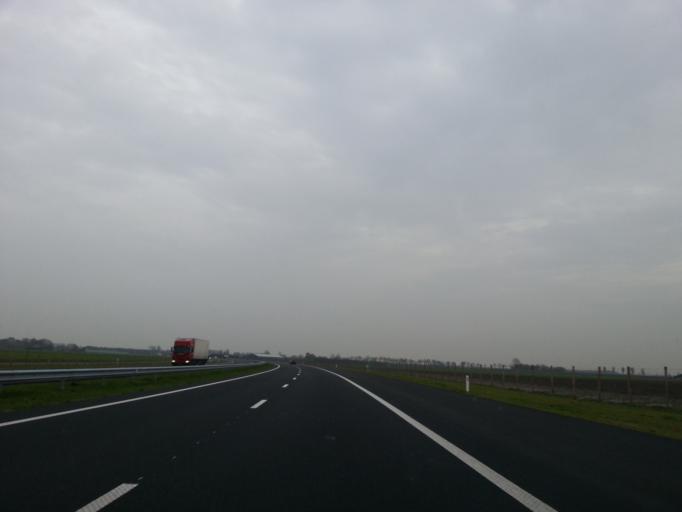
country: NL
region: North Brabant
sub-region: Gemeente Steenbergen
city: Welberg
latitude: 51.5973
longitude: 4.3431
